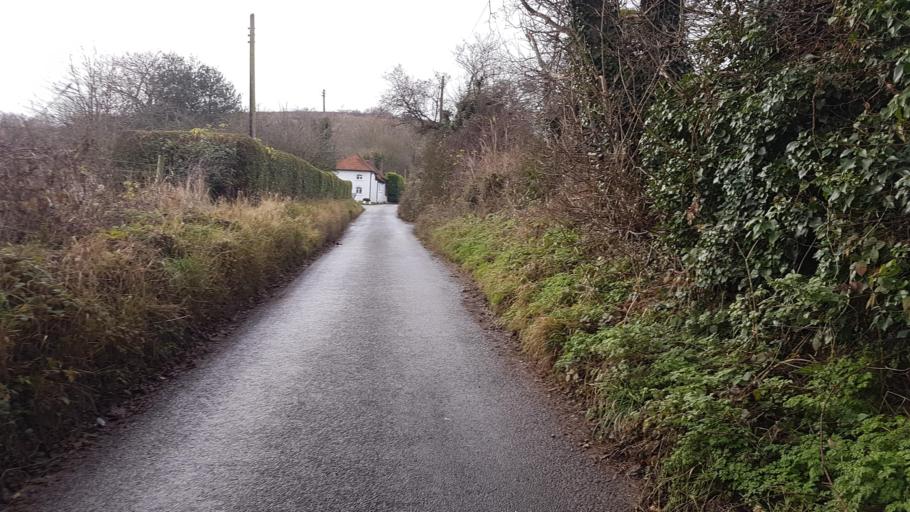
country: GB
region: England
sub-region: West Sussex
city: Steyning
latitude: 50.8849
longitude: -0.3373
